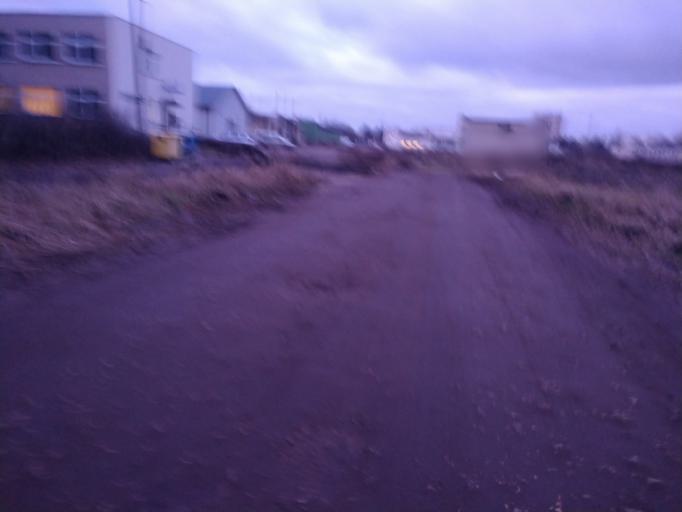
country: LV
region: Stopini
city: Ulbroka
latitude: 56.9538
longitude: 24.2318
